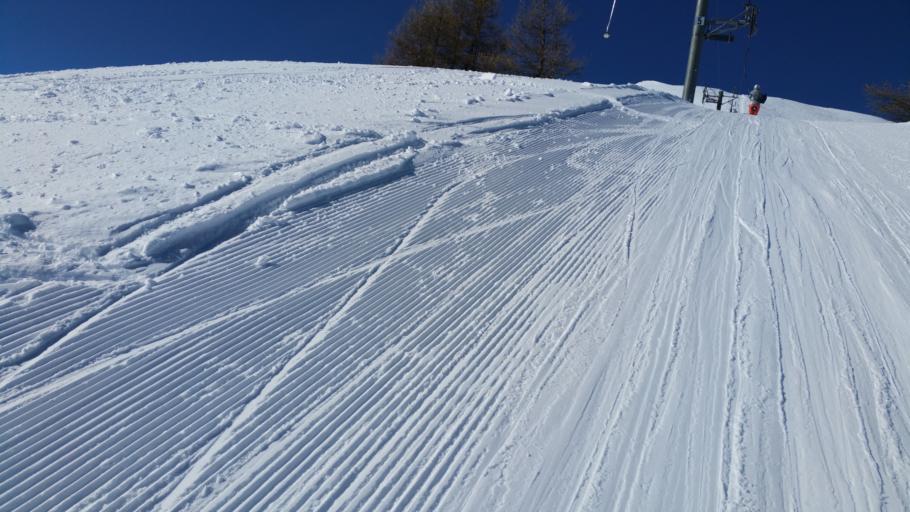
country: FR
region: Rhone-Alpes
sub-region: Departement de la Savoie
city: Valloire
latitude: 45.2052
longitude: 6.4008
